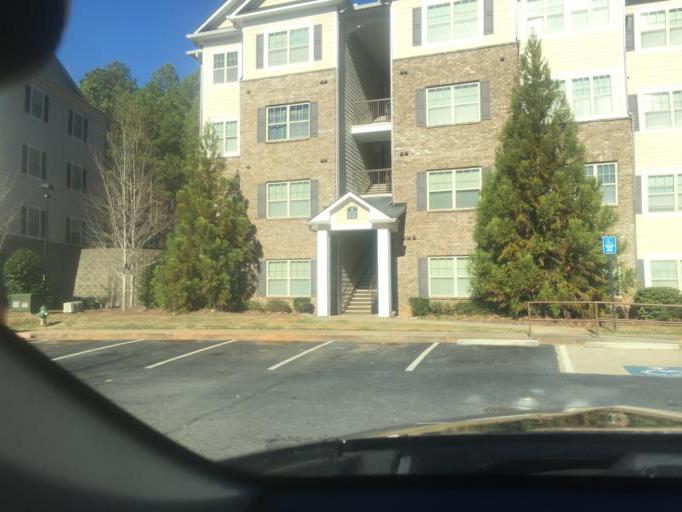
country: US
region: Georgia
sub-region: Fulton County
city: Fairburn
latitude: 33.6132
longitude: -84.6061
